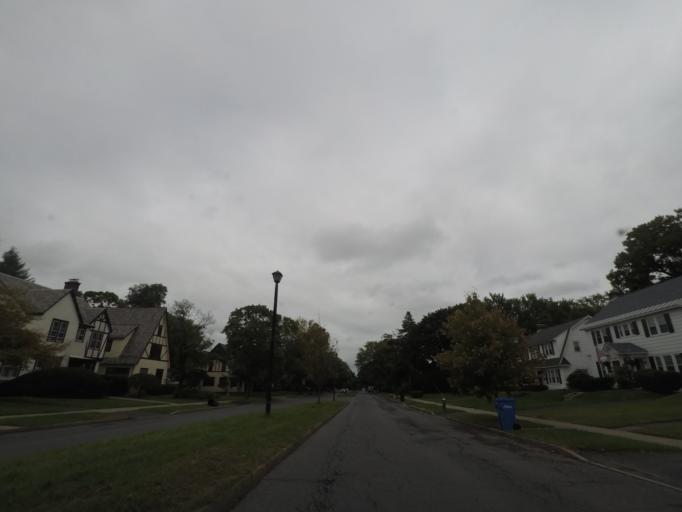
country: US
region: New York
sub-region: Albany County
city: West Albany
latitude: 42.6562
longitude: -73.7977
